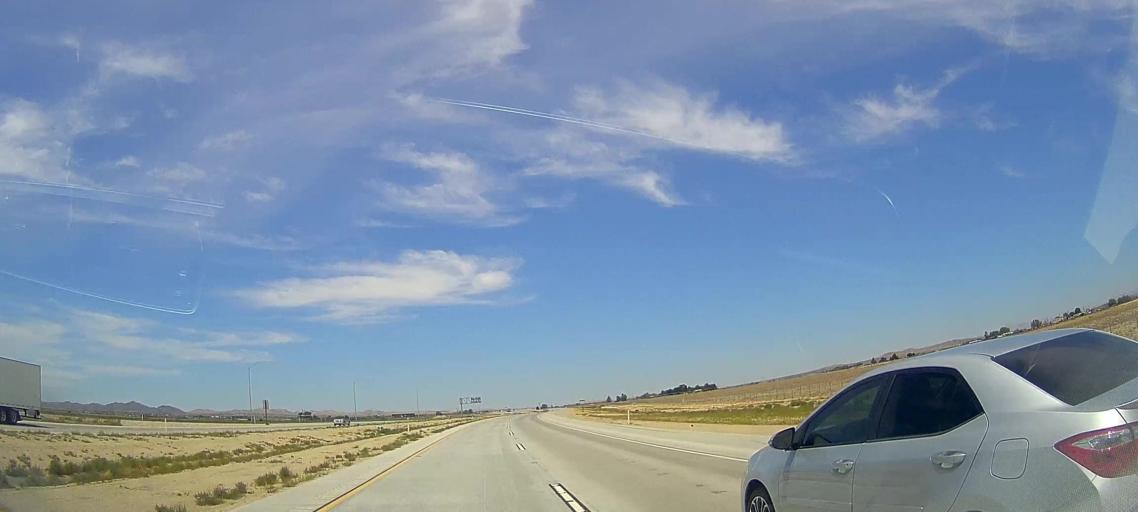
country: US
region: California
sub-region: San Bernardino County
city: Lenwood
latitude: 34.9151
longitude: -117.1237
